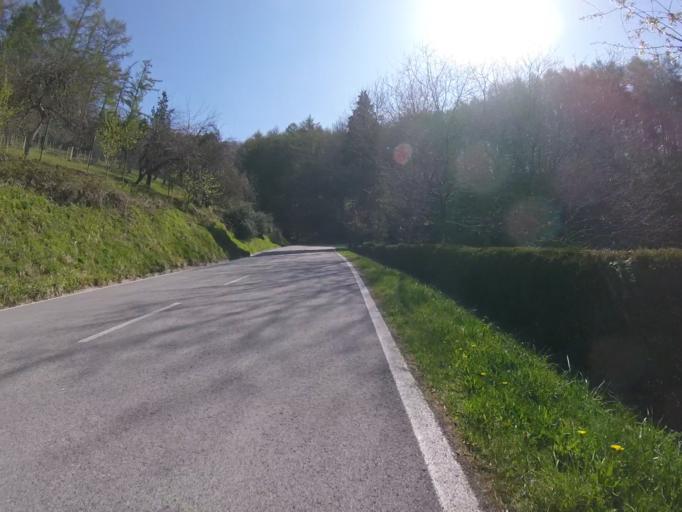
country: ES
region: Navarre
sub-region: Provincia de Navarra
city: Leitza
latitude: 43.0902
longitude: -1.8883
